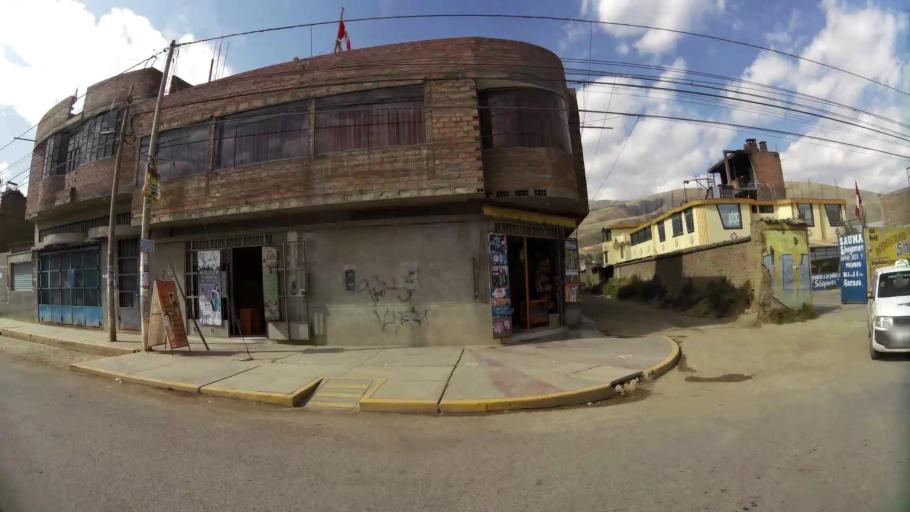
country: PE
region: Junin
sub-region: Provincia de Huancayo
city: Huancayo
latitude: -12.0893
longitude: -75.1974
